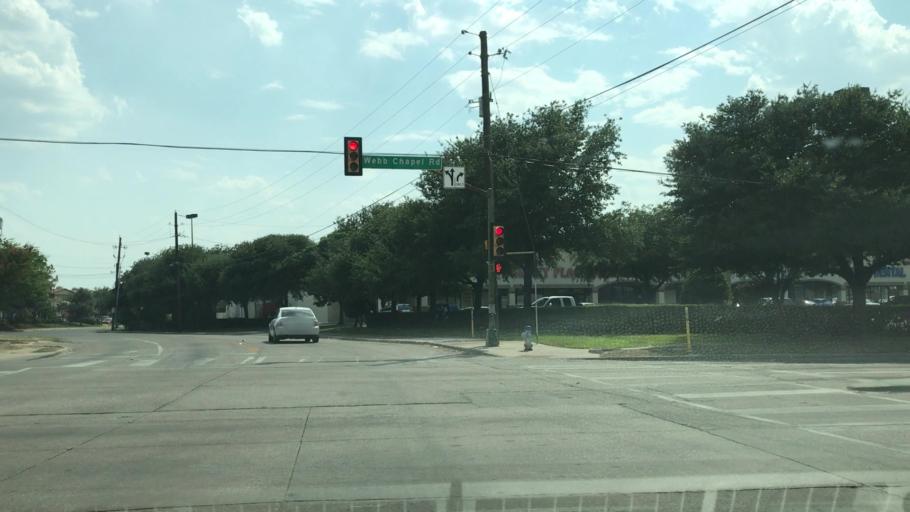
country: US
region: Texas
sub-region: Dallas County
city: University Park
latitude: 32.8650
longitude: -96.8623
